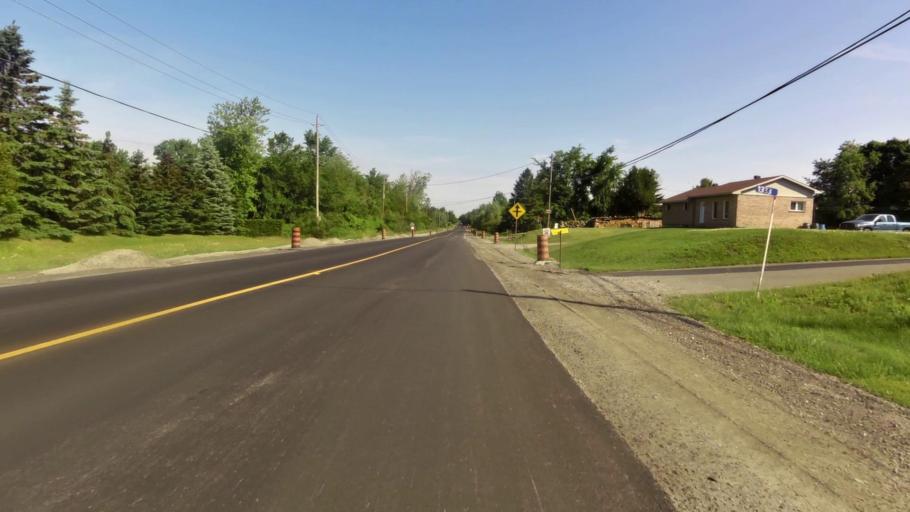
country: CA
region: Ontario
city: Ottawa
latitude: 45.2529
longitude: -75.5918
